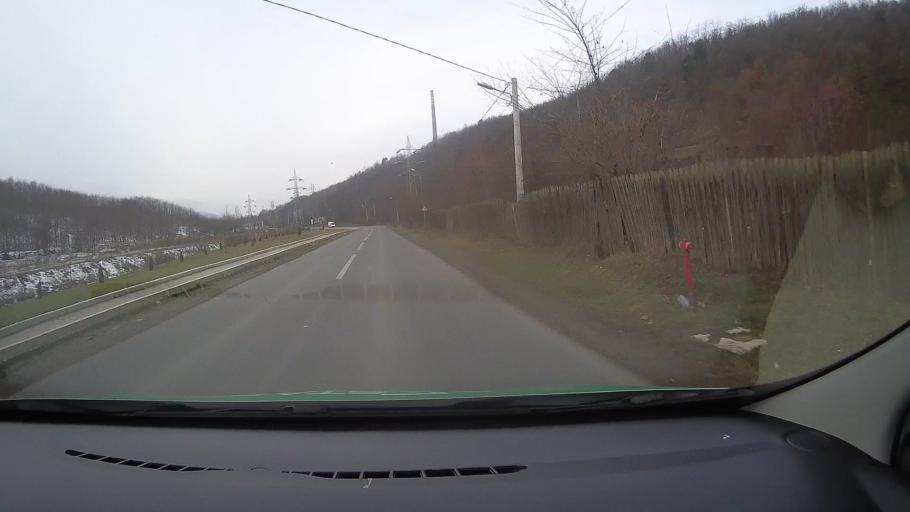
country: RO
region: Alba
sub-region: Oras Zlatna
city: Zlatna
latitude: 46.1035
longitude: 23.2460
